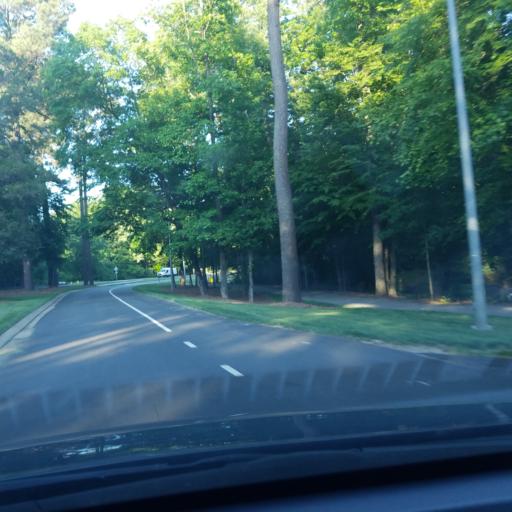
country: US
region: North Carolina
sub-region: Durham County
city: Durham
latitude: 35.9225
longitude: -78.9540
